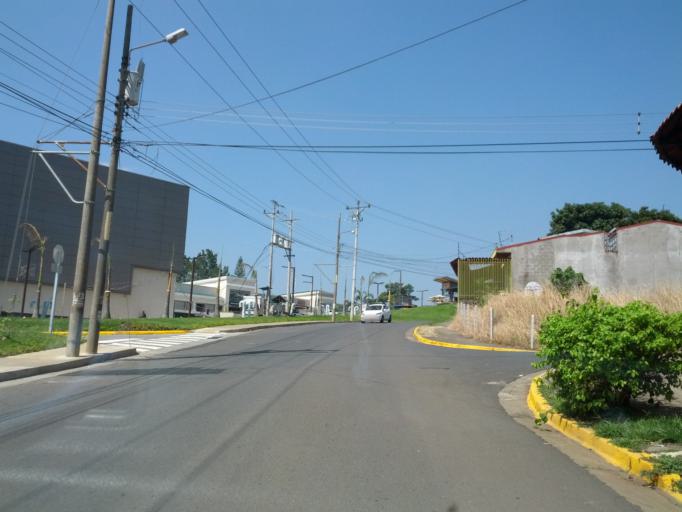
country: CR
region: Alajuela
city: Alajuela
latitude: 10.0117
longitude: -84.2053
